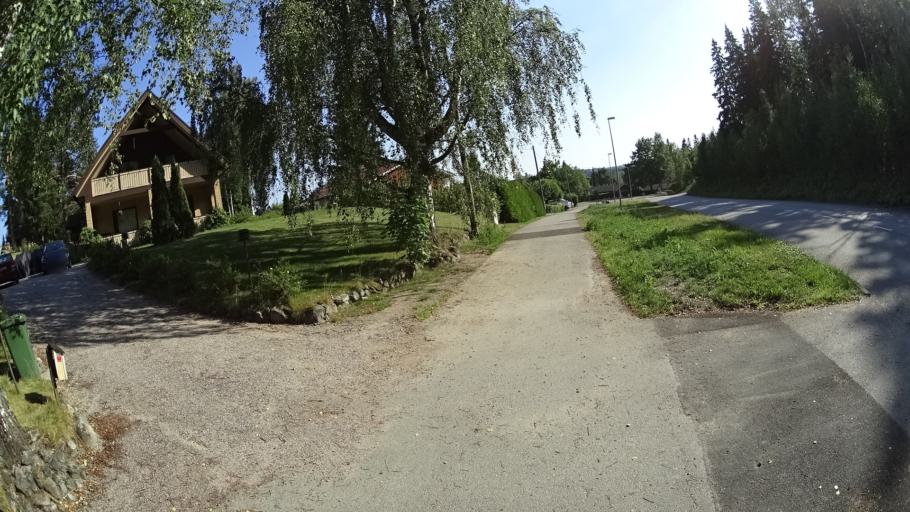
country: FI
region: Uusimaa
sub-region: Porvoo
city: Porvoo
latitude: 60.4115
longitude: 25.6500
